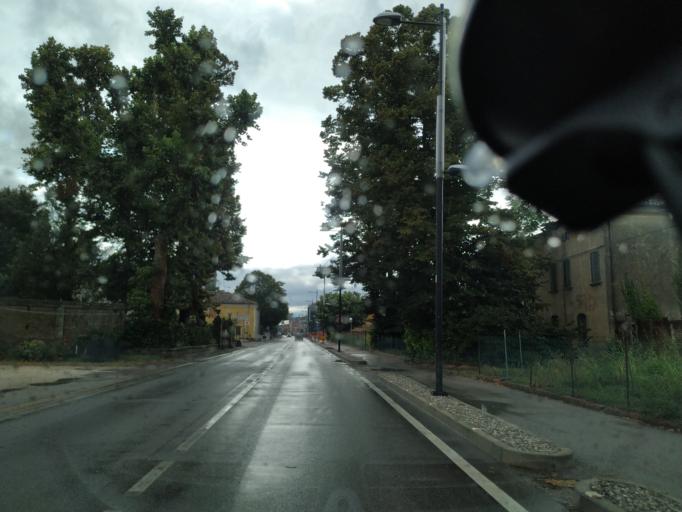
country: IT
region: Emilia-Romagna
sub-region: Provincia di Ferrara
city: Mirabello
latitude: 44.8282
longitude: 11.4639
